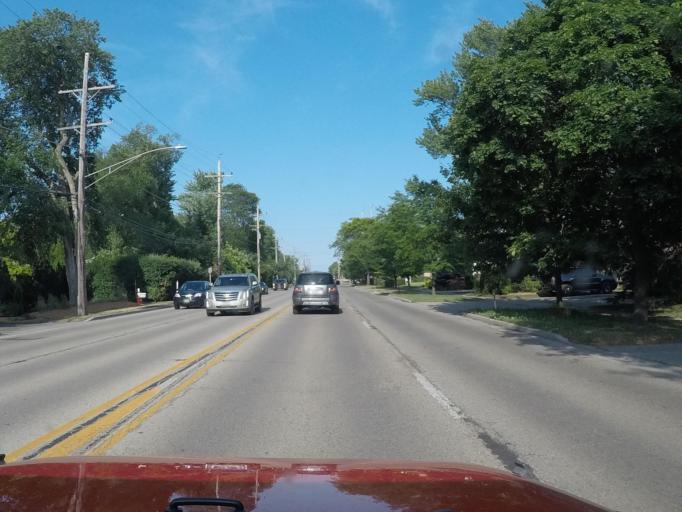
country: US
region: Illinois
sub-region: Cook County
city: Glenview
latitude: 42.0796
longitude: -87.7695
